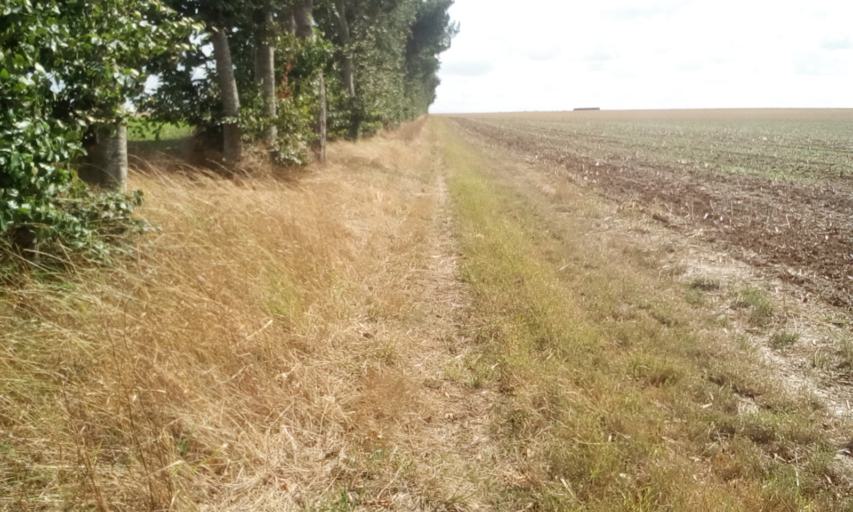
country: FR
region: Lower Normandy
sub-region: Departement du Calvados
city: Saint-Sylvain
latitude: 49.0846
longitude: -0.1973
